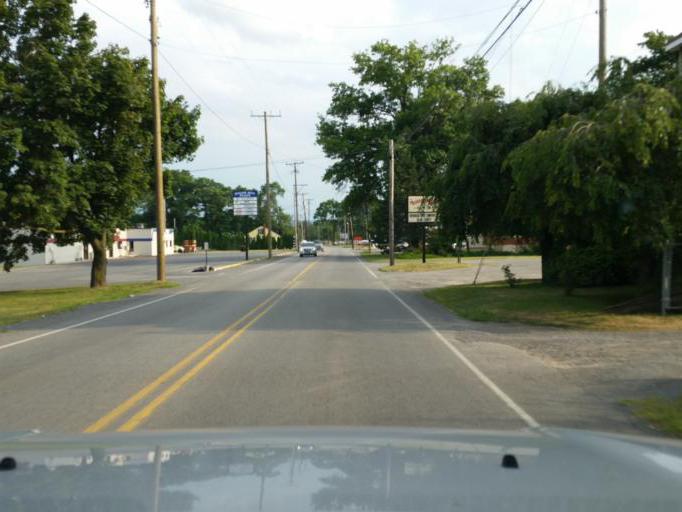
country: US
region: Pennsylvania
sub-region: Blair County
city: Duncansville
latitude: 40.4626
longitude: -78.4271
